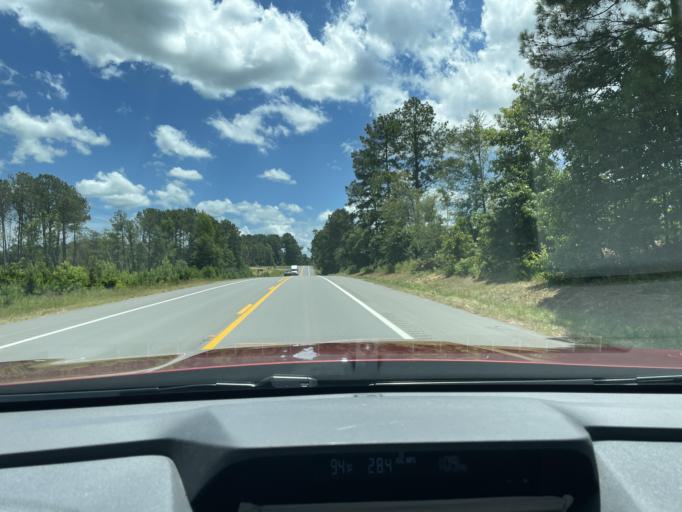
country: US
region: Arkansas
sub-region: Drew County
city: Monticello
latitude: 33.7331
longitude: -91.8158
